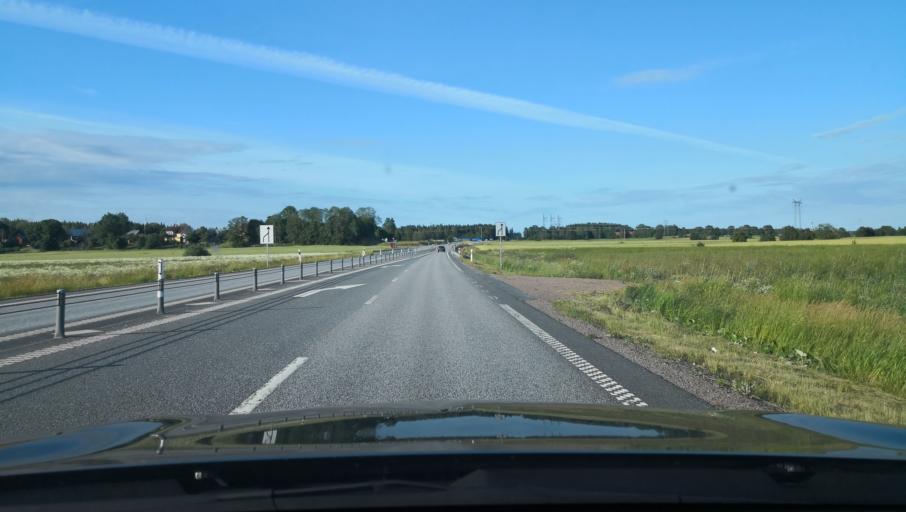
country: SE
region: Uppsala
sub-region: Osthammars Kommun
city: Osterbybruk
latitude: 60.0203
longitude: 17.9847
